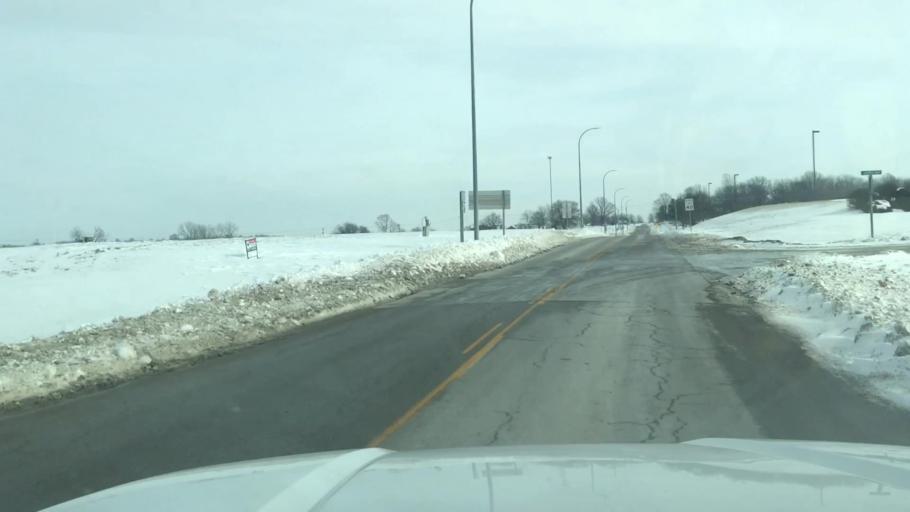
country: US
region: Missouri
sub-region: Clinton County
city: Cameron
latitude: 39.7316
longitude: -94.2195
